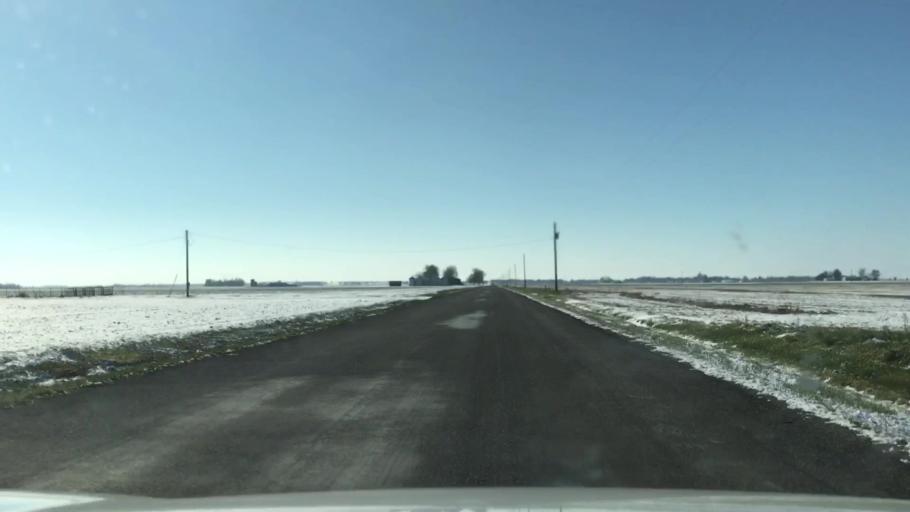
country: US
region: Illinois
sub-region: Washington County
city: Okawville
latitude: 38.4247
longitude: -89.4778
